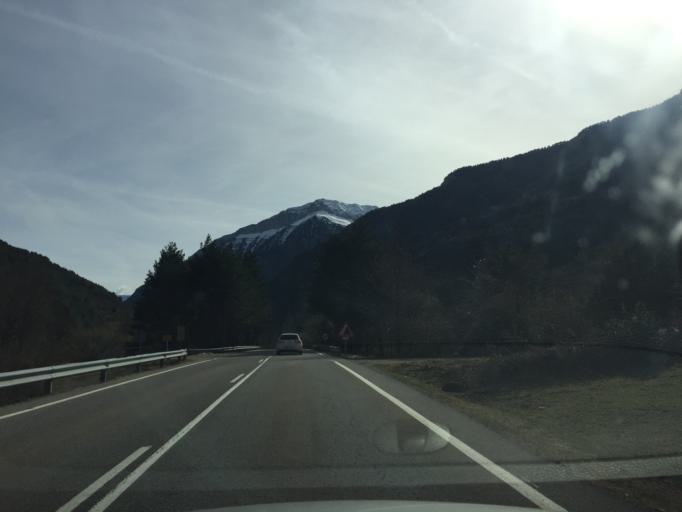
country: ES
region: Aragon
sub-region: Provincia de Huesca
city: Bielsa
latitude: 42.6587
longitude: 0.2092
